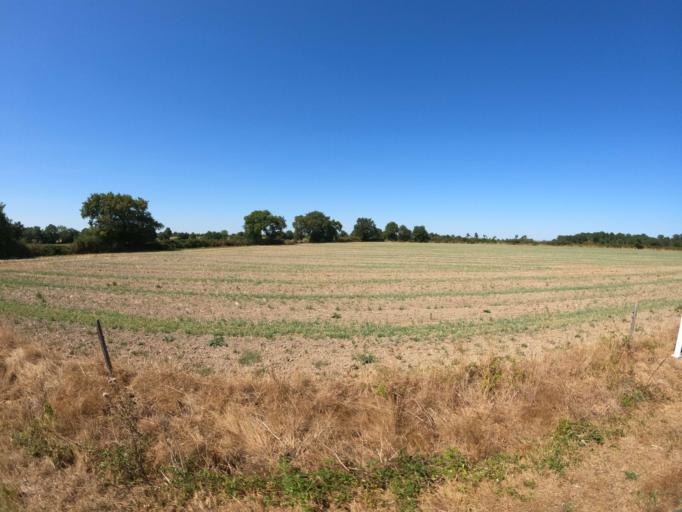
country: FR
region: Pays de la Loire
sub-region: Departement de la Vendee
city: La Boissiere-de-Montaigu
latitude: 46.9600
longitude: -1.1577
